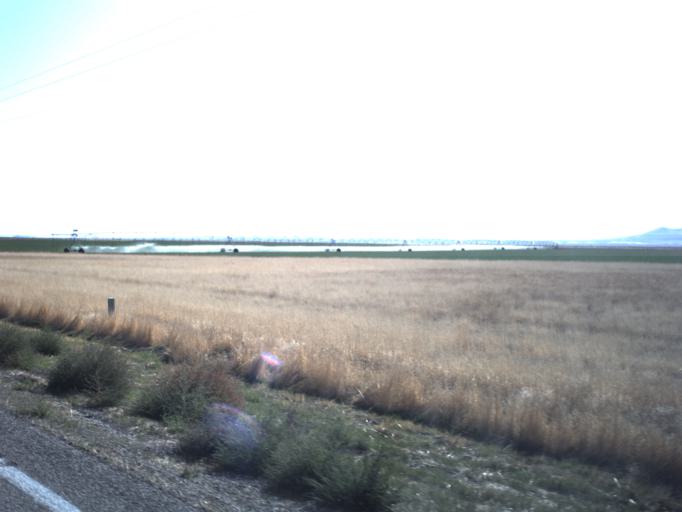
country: US
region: Utah
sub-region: Millard County
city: Delta
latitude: 39.1951
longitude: -112.4100
